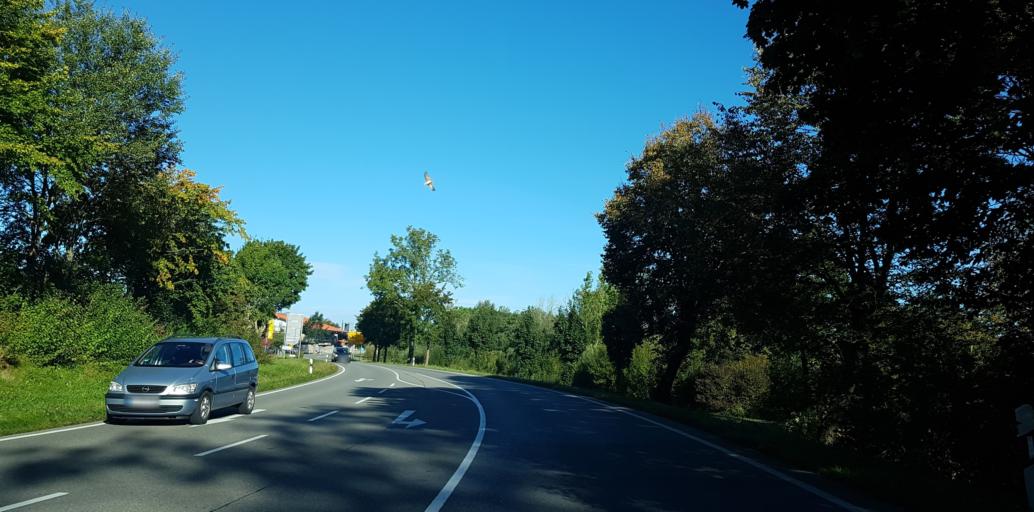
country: DE
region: Baden-Wuerttemberg
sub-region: Tuebingen Region
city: Bad Wurzach
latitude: 47.9001
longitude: 9.8975
